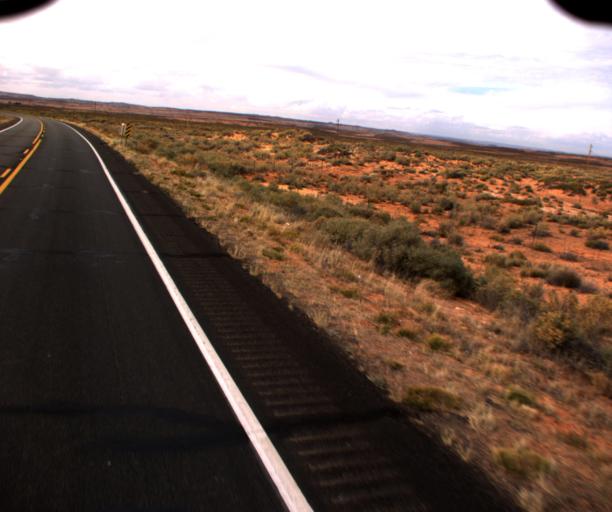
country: US
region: Arizona
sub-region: Apache County
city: Many Farms
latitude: 36.9401
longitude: -109.6417
